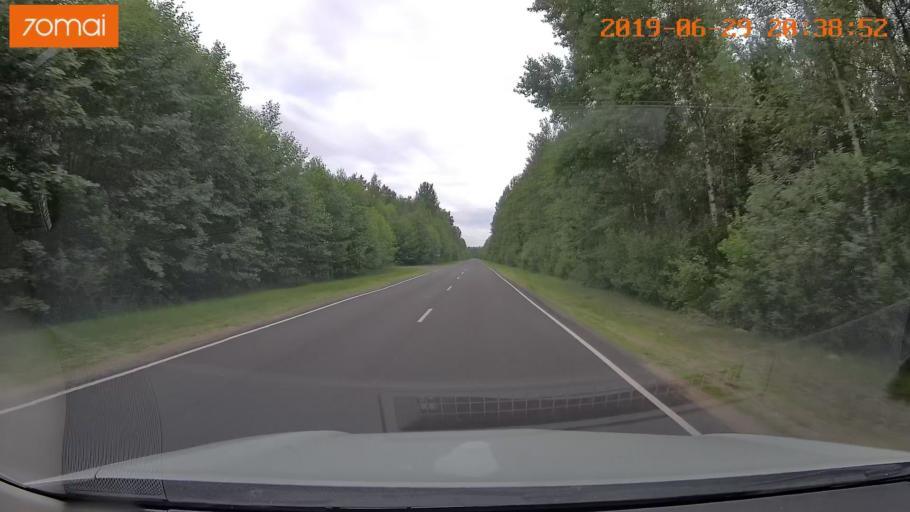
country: BY
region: Brest
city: Hantsavichy
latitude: 52.5553
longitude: 26.3638
